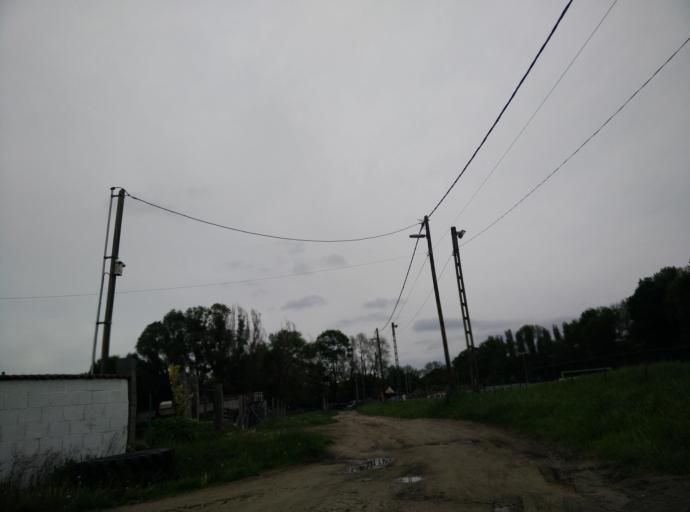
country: HU
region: Pest
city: Fot
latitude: 47.6090
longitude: 19.1869
